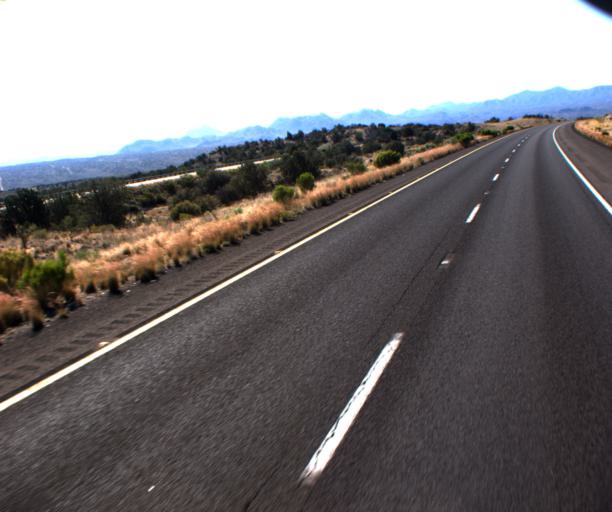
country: US
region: Arizona
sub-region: Mohave County
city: New Kingman-Butler
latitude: 35.1386
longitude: -113.6735
